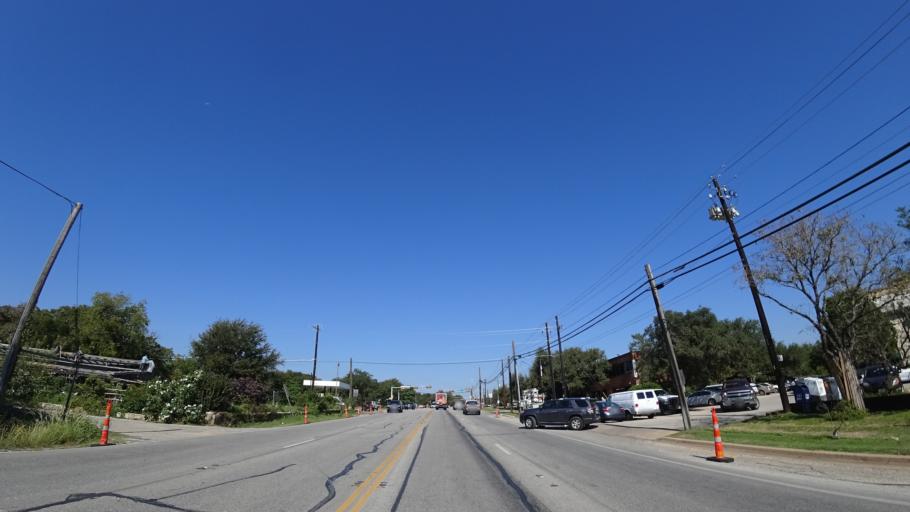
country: US
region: Texas
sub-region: Travis County
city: Rollingwood
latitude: 30.2777
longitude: -97.8050
